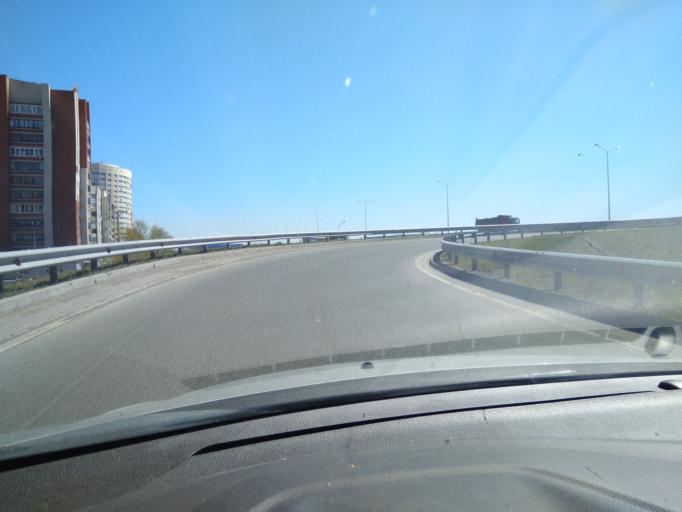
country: RU
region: Tjumen
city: Tyumen
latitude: 57.1204
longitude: 65.5215
